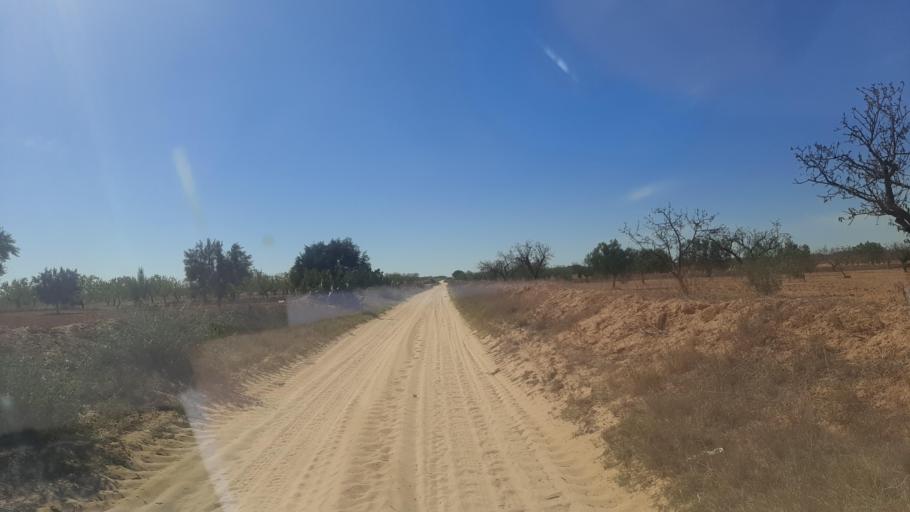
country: TN
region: Safaqis
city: Sfax
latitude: 34.8215
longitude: 10.5522
